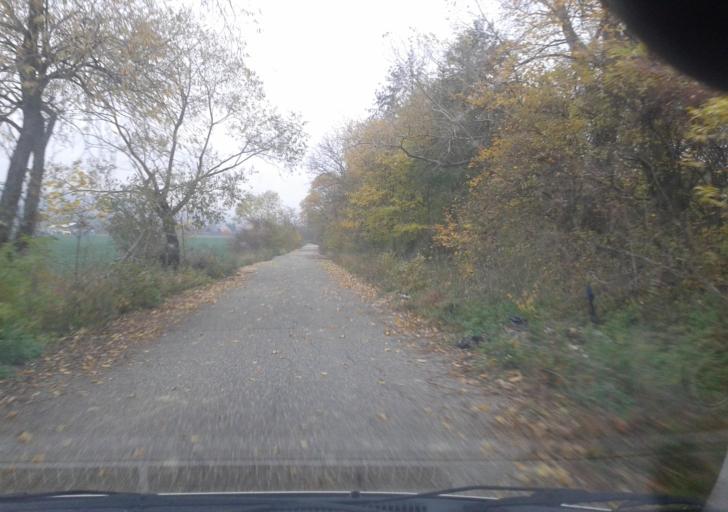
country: SK
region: Banskobystricky
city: Nova Bana
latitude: 48.3120
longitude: 18.7015
